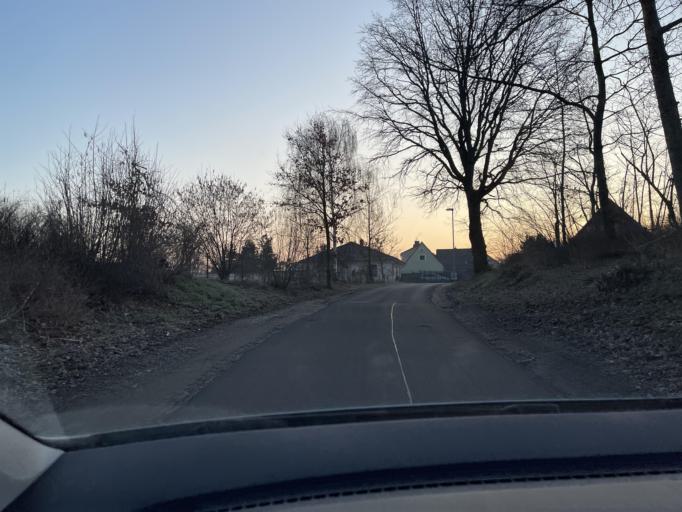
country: DE
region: Brandenburg
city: Gross Kreutz
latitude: 52.3887
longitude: 12.6968
